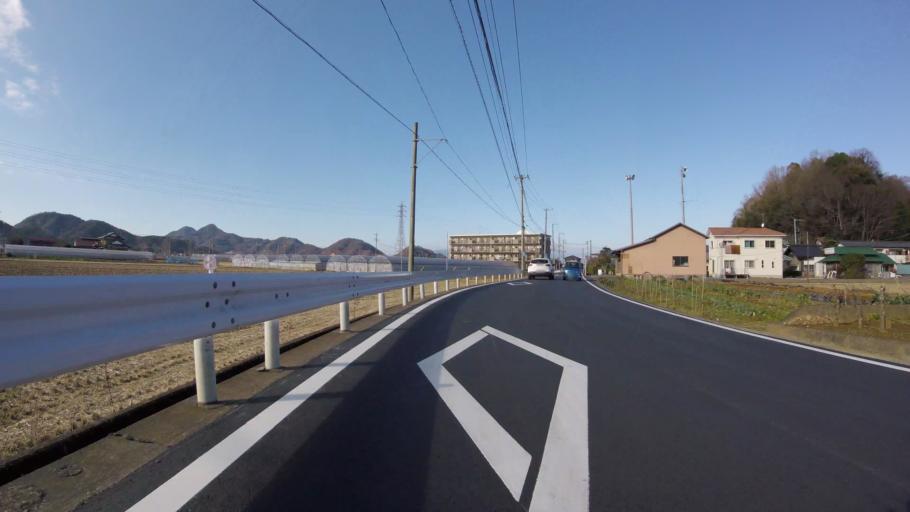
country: JP
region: Shizuoka
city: Mishima
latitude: 35.0479
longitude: 138.9532
